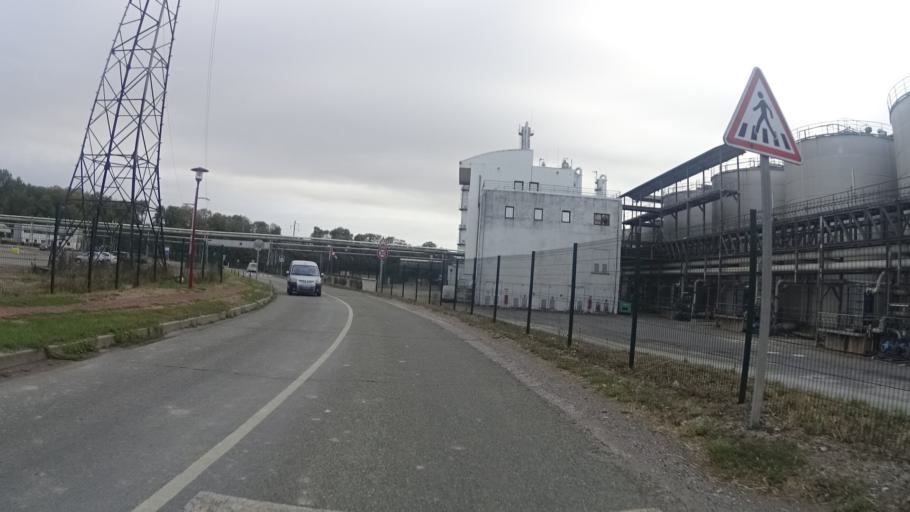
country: FR
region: Picardie
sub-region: Departement de l'Aisne
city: Origny-Sainte-Benoite
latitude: 49.8367
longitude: 3.4751
